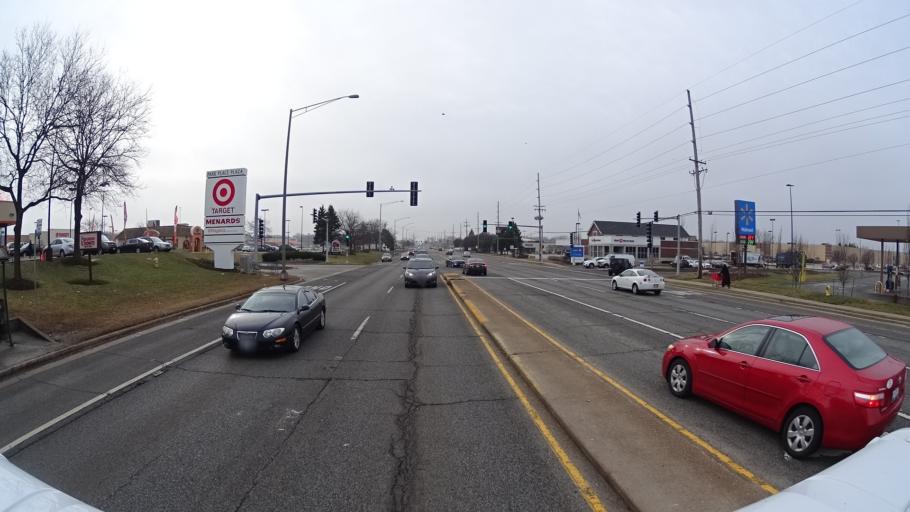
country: US
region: Illinois
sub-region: Cook County
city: East Hazel Crest
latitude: 41.5698
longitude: -87.6365
